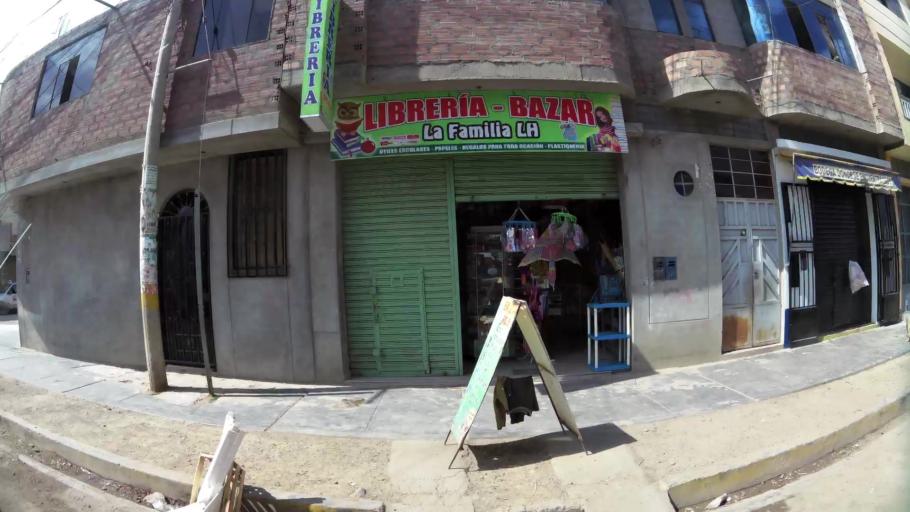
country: PE
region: Junin
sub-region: Provincia de Huancayo
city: Huancayo
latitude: -12.0915
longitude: -75.2023
